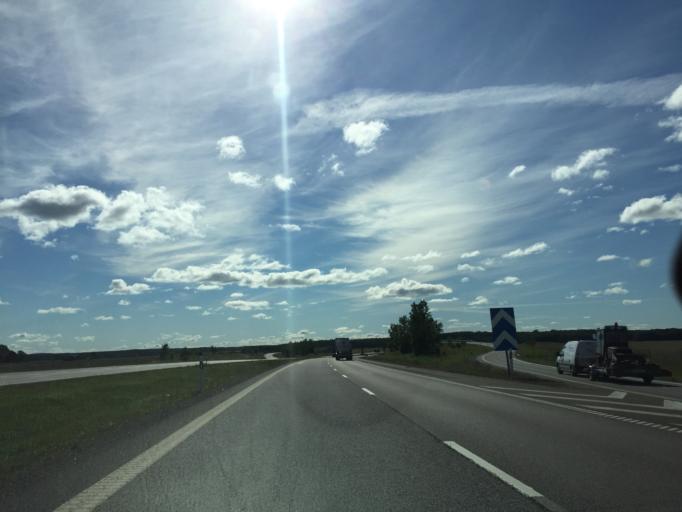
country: SE
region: Vaestmanland
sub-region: Arboga Kommun
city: Arboga
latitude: 59.4370
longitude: 15.8984
